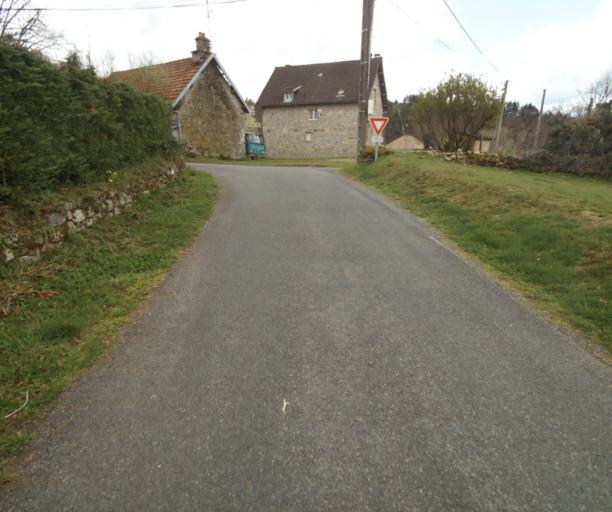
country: FR
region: Limousin
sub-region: Departement de la Correze
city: Correze
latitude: 45.3276
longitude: 1.9372
